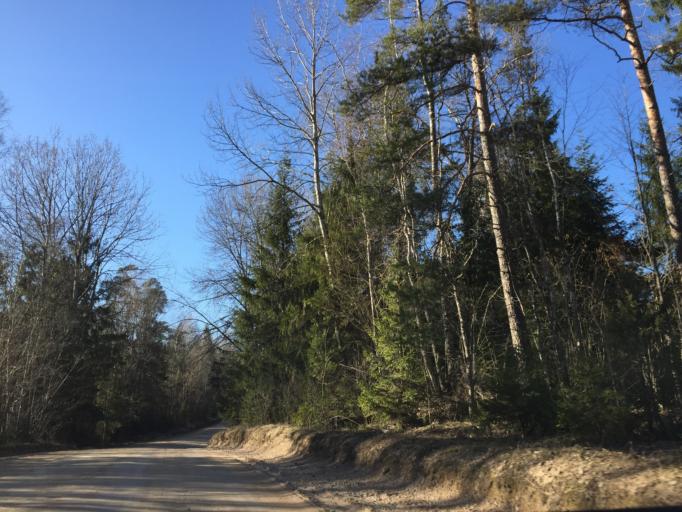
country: LV
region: Ropazu
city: Ropazi
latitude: 56.9177
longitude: 24.7138
